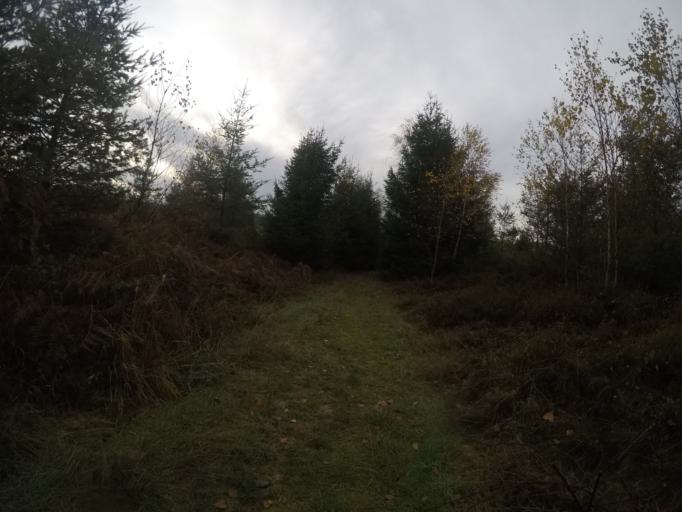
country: BE
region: Wallonia
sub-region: Province du Luxembourg
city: Habay-la-Vieille
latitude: 49.7425
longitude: 5.6046
